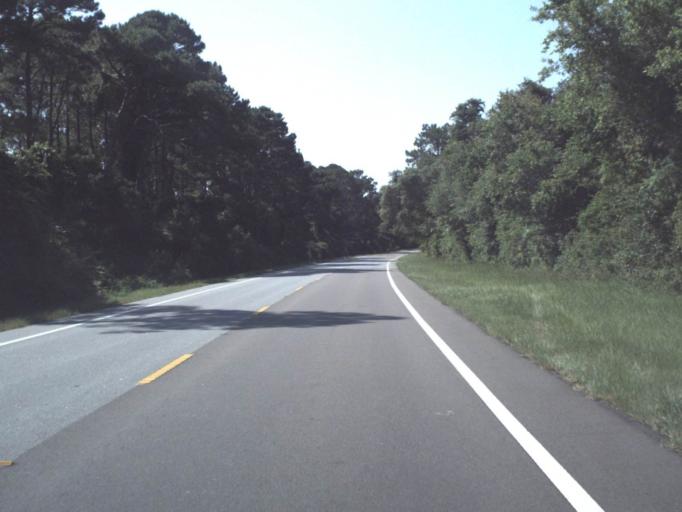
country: US
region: Florida
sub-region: Duval County
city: Atlantic Beach
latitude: 30.4894
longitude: -81.4413
